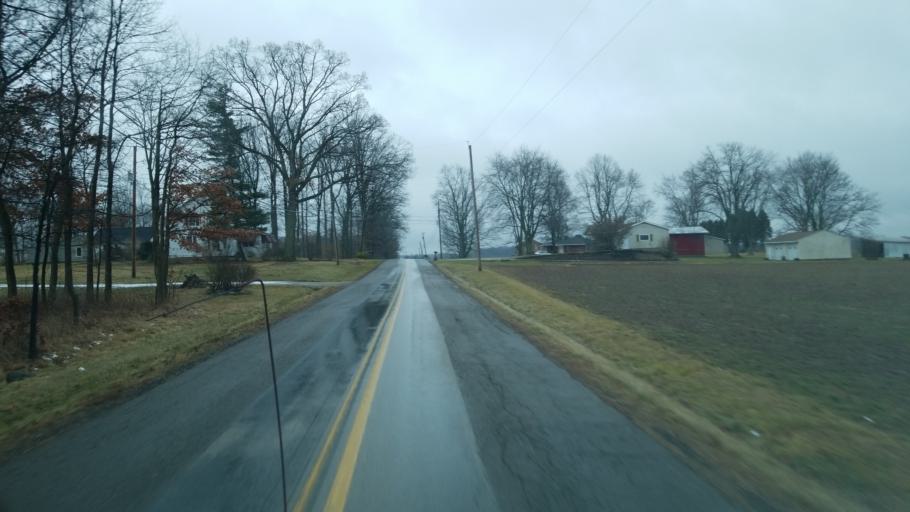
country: US
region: Ohio
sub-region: Wayne County
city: Smithville
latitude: 40.8340
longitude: -81.8615
